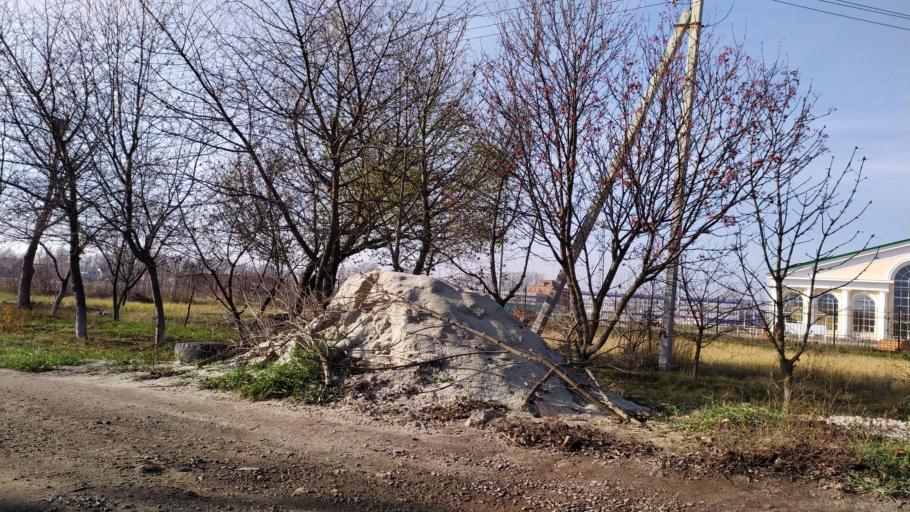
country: RU
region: Kursk
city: Kursk
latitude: 51.6410
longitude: 36.1308
